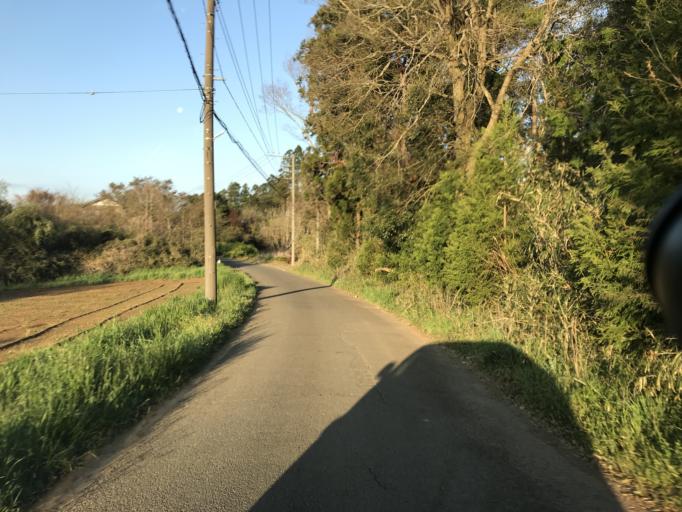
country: JP
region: Chiba
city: Yokaichiba
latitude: 35.7838
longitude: 140.5408
